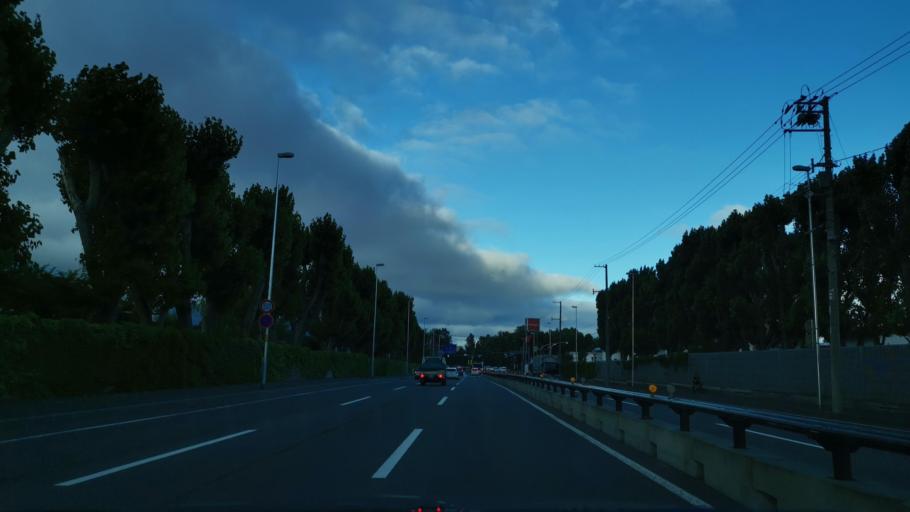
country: JP
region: Hokkaido
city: Sapporo
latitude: 43.0808
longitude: 141.3270
